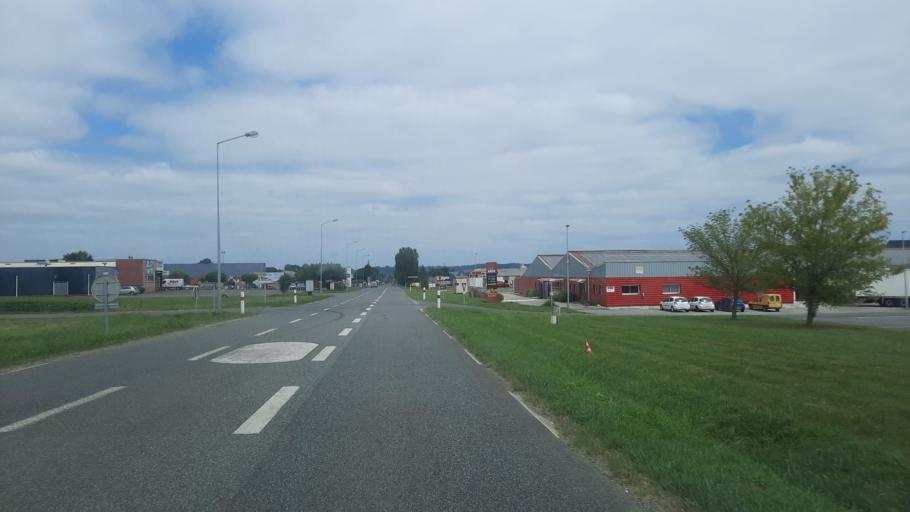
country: FR
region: Midi-Pyrenees
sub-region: Departement des Hautes-Pyrenees
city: Trie-sur-Baise
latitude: 43.3105
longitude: 0.3586
